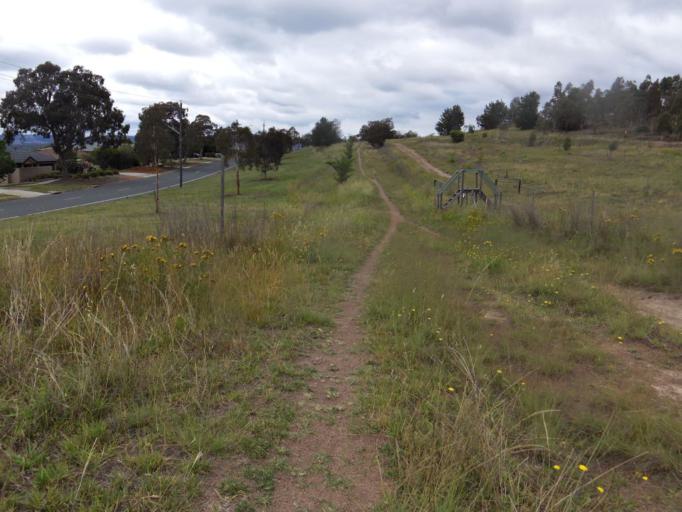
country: AU
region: Australian Capital Territory
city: Macquarie
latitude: -35.3381
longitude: 149.0264
